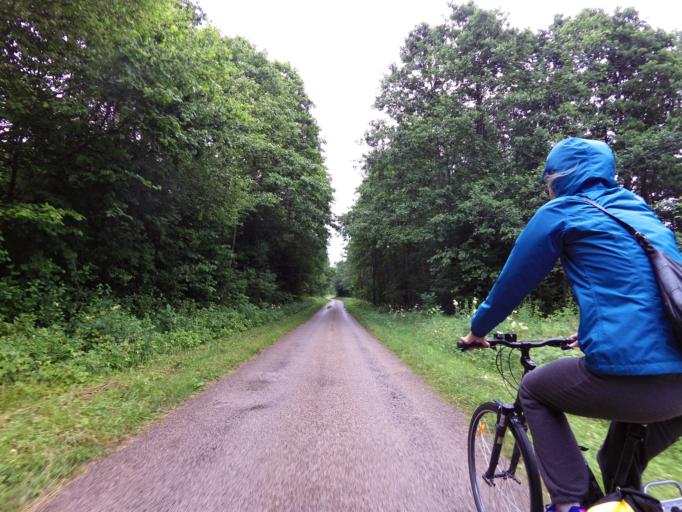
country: EE
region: Laeaene
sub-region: Vormsi vald
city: Hullo
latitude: 59.0193
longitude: 23.3153
